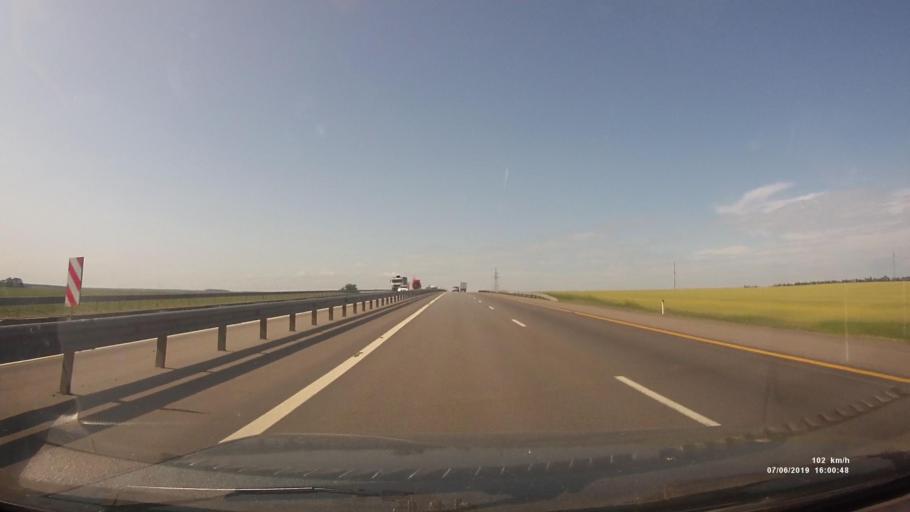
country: RU
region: Rostov
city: Zverevo
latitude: 47.9547
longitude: 40.2178
